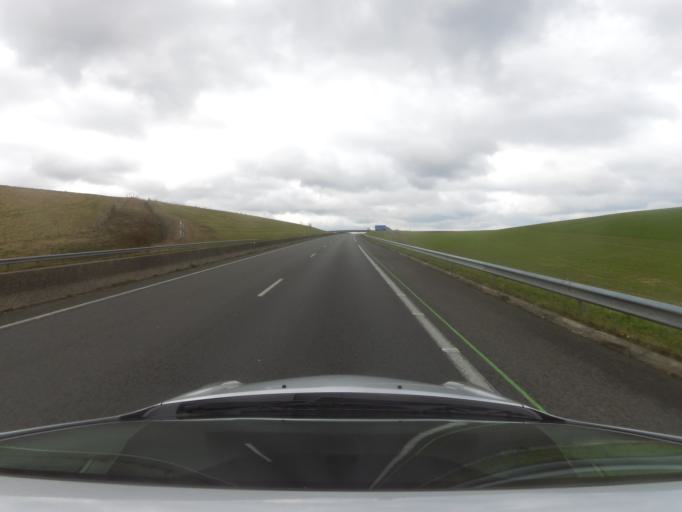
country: FR
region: Nord-Pas-de-Calais
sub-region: Departement du Pas-de-Calais
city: Neufchatel-Hardelot
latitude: 50.5992
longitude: 1.6498
